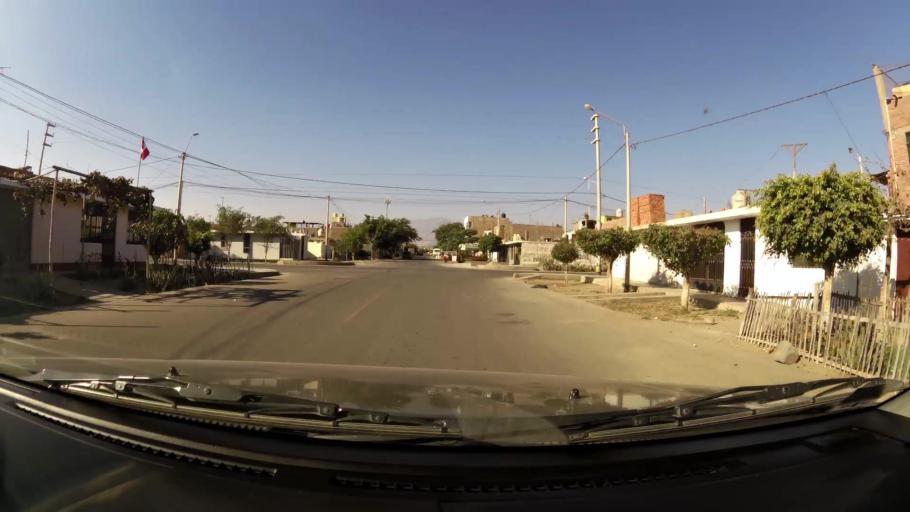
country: PE
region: Ica
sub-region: Provincia de Ica
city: La Tinguina
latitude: -14.0452
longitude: -75.7055
